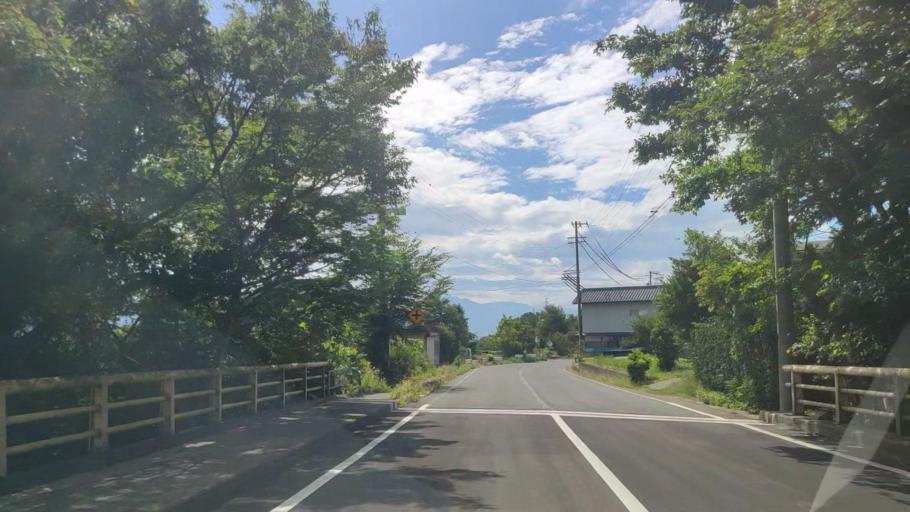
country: JP
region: Nagano
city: Nakano
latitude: 36.7432
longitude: 138.3089
